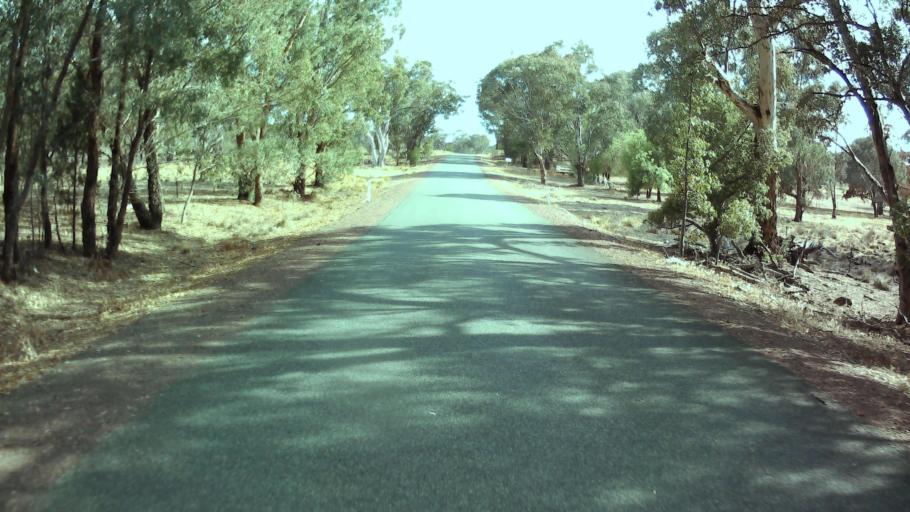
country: AU
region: New South Wales
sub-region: Weddin
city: Grenfell
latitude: -33.8159
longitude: 148.2918
